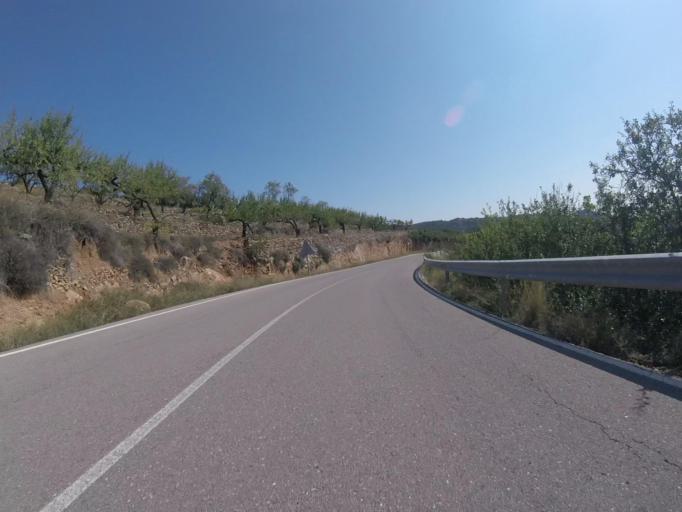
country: ES
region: Valencia
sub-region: Provincia de Castello
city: Benafigos
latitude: 40.2644
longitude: -0.2193
